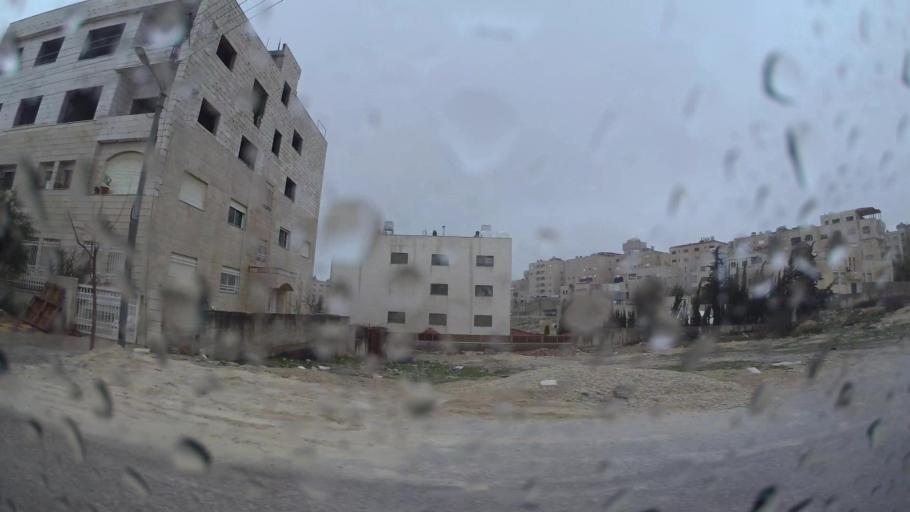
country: JO
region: Amman
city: Al Jubayhah
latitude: 32.0140
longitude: 35.8890
